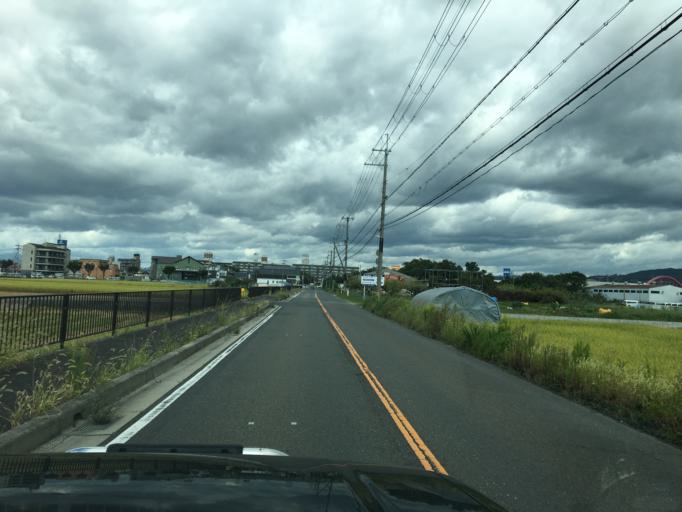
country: JP
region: Kyoto
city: Tanabe
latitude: 34.8156
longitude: 135.7884
